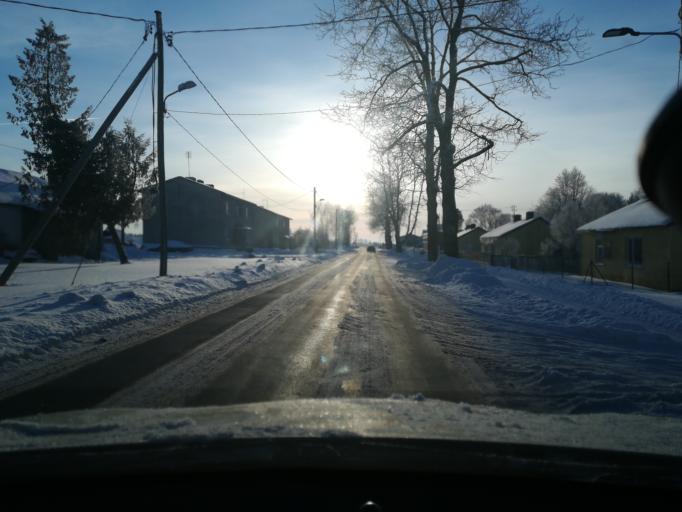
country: EE
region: Harju
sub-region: Saue linn
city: Saue
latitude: 59.3433
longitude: 24.5569
